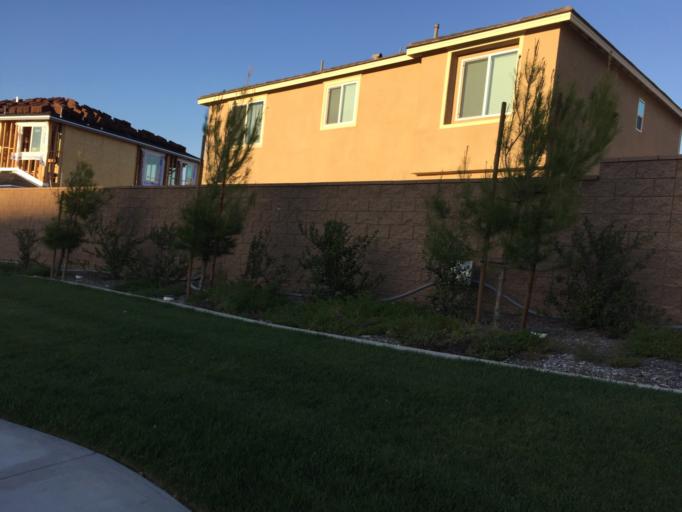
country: US
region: California
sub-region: Riverside County
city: Home Gardens
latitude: 33.8967
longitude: -117.4640
